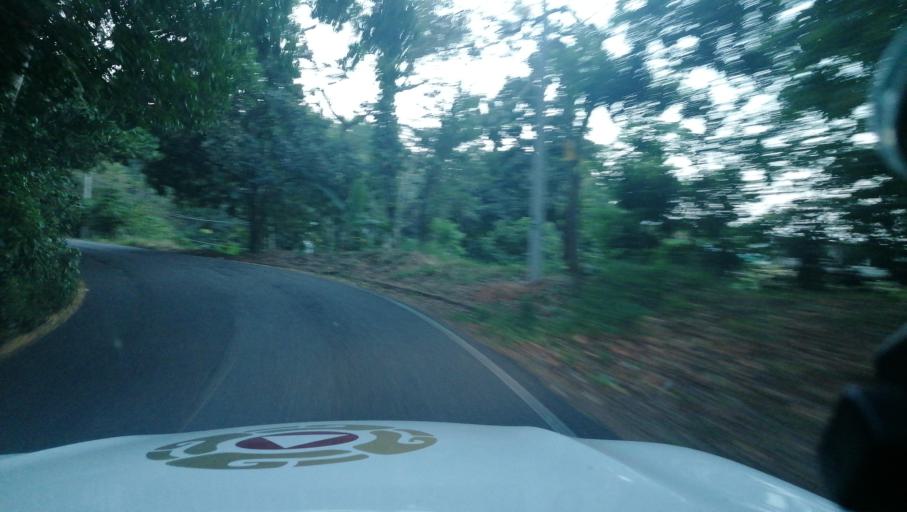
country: MX
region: Chiapas
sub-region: Cacahoatan
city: Benito Juarez
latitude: 15.0345
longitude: -92.2427
